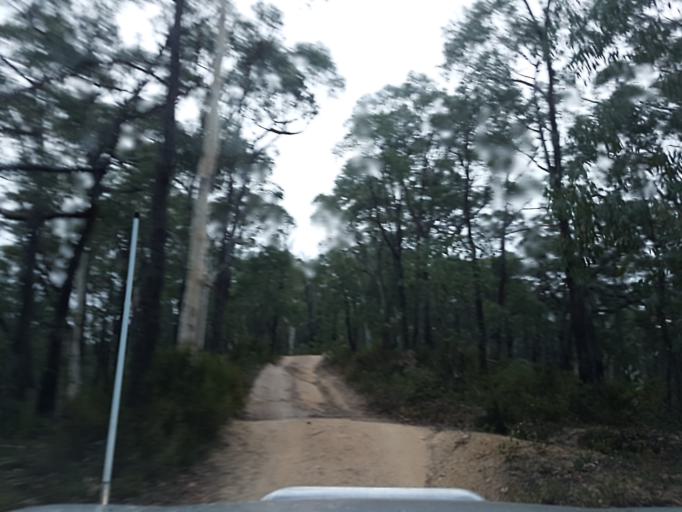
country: AU
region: New South Wales
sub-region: Snowy River
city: Jindabyne
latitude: -36.8579
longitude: 148.2326
